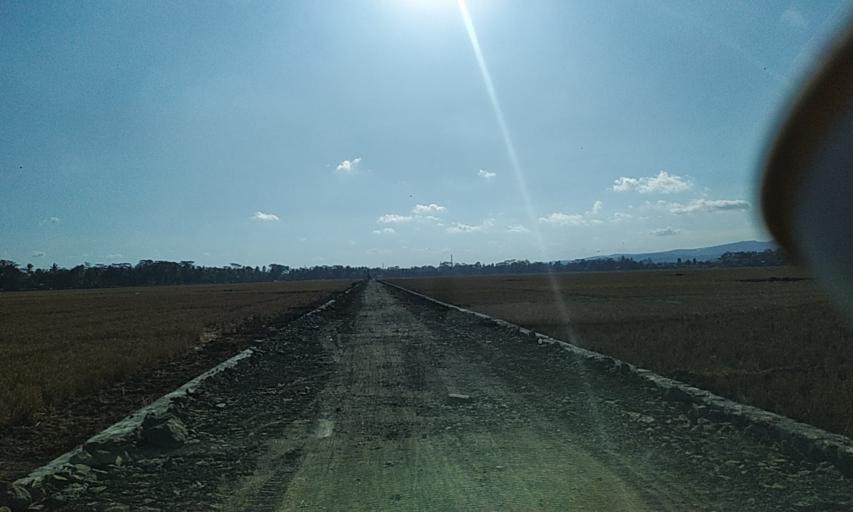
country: ID
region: Central Java
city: Krikil
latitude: -7.6239
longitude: 109.1389
